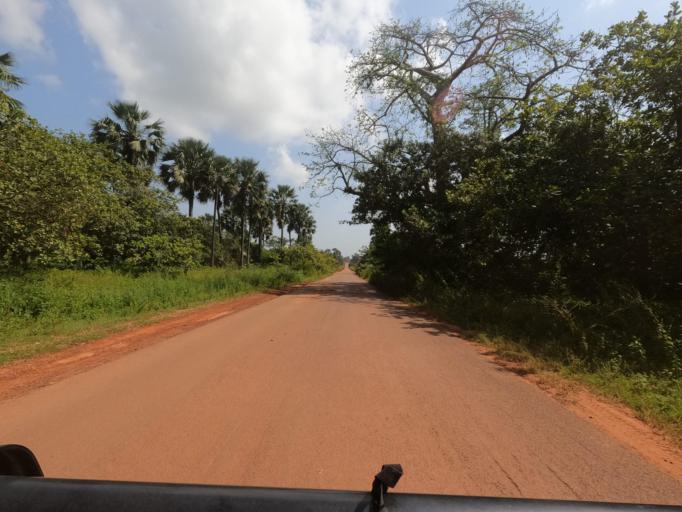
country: GW
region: Cacheu
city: Canchungo
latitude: 12.2851
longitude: -15.7813
